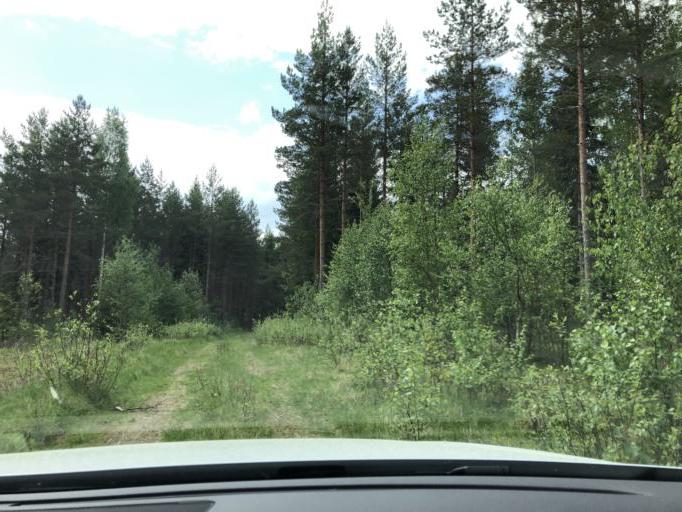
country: SE
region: Dalarna
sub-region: Avesta Kommun
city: Horndal
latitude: 60.2207
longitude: 16.5056
